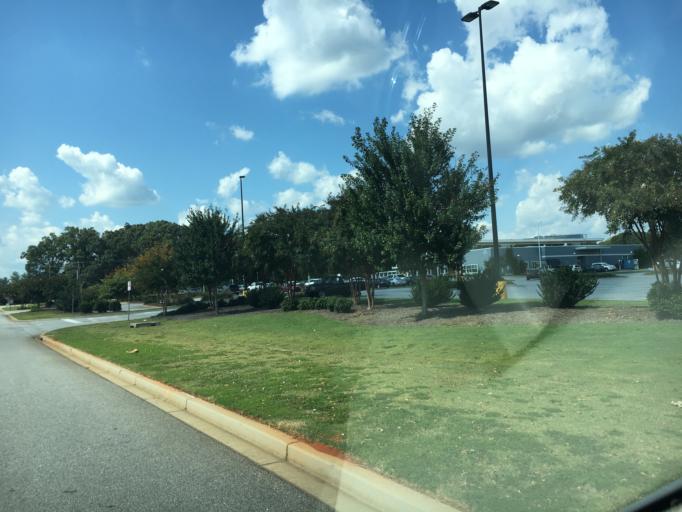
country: US
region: South Carolina
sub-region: Anderson County
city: Powdersville
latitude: 34.7888
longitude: -82.4800
